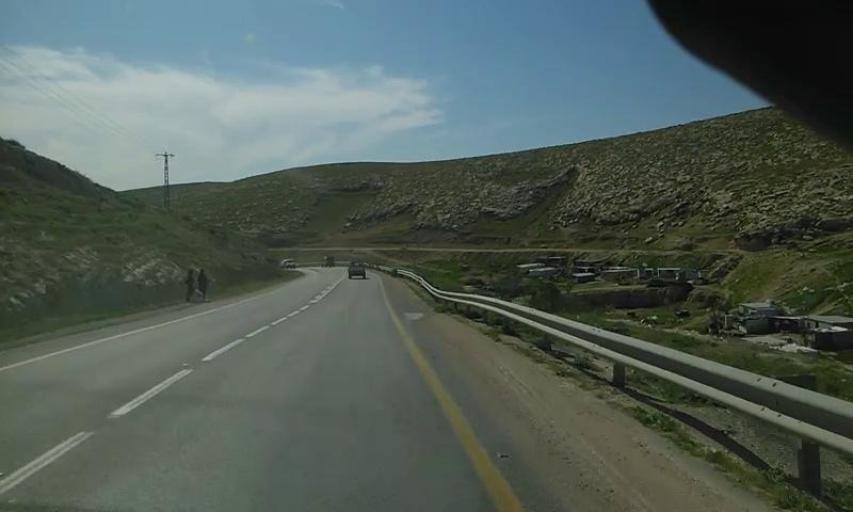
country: PS
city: Az Za`ayyim
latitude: 31.8076
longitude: 35.3080
